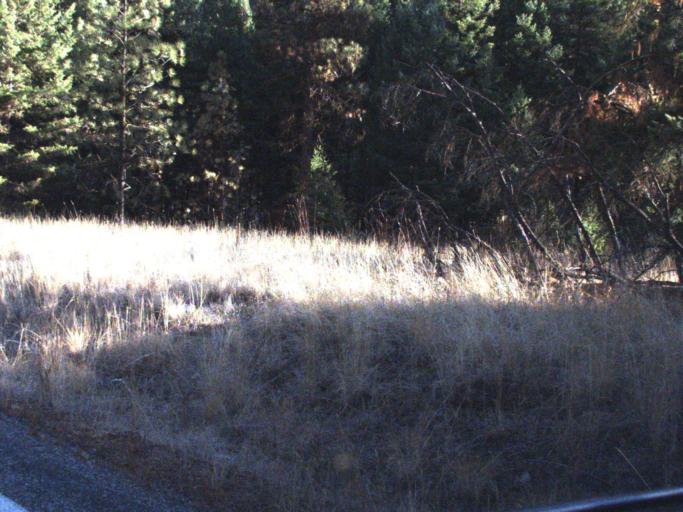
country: US
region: Washington
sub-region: Ferry County
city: Republic
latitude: 48.3589
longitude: -118.7410
